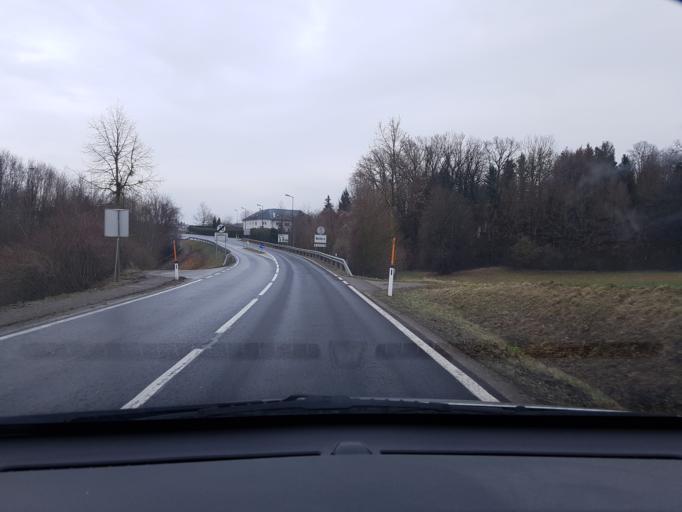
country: AT
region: Upper Austria
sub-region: Steyr Stadt
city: Steyr
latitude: 48.0800
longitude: 14.3722
